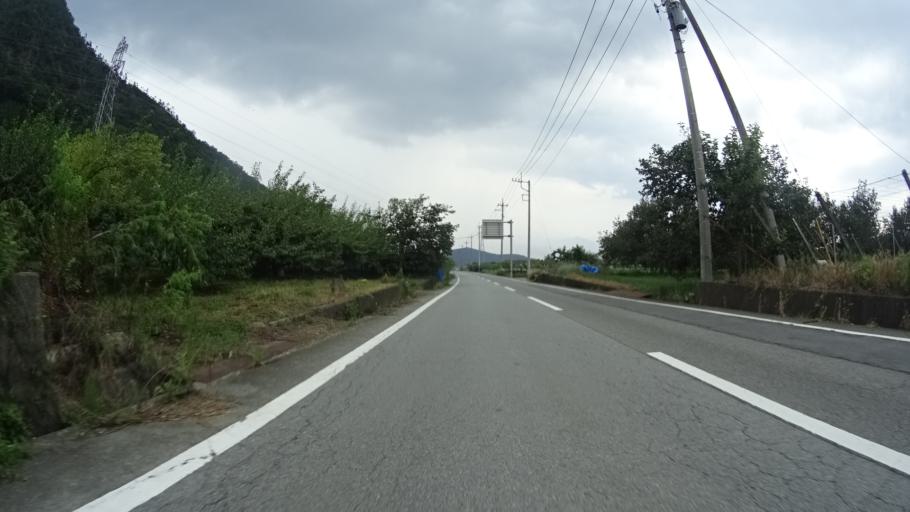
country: JP
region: Yamanashi
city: Enzan
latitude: 35.7376
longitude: 138.7214
